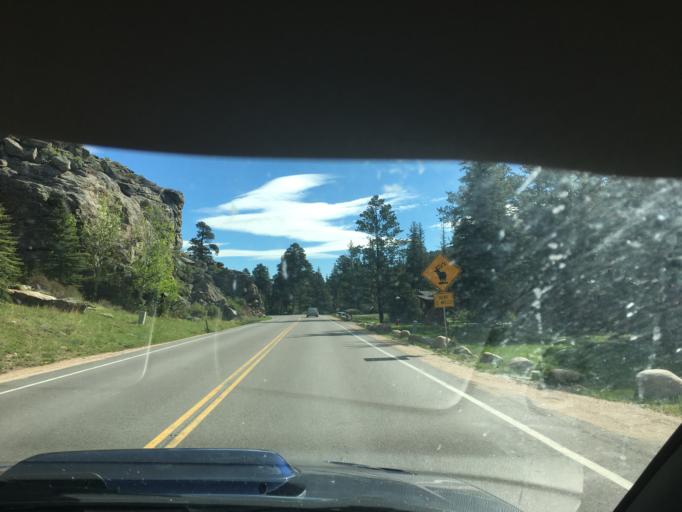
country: US
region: Colorado
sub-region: Larimer County
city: Estes Park
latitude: 40.3516
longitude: -105.5654
